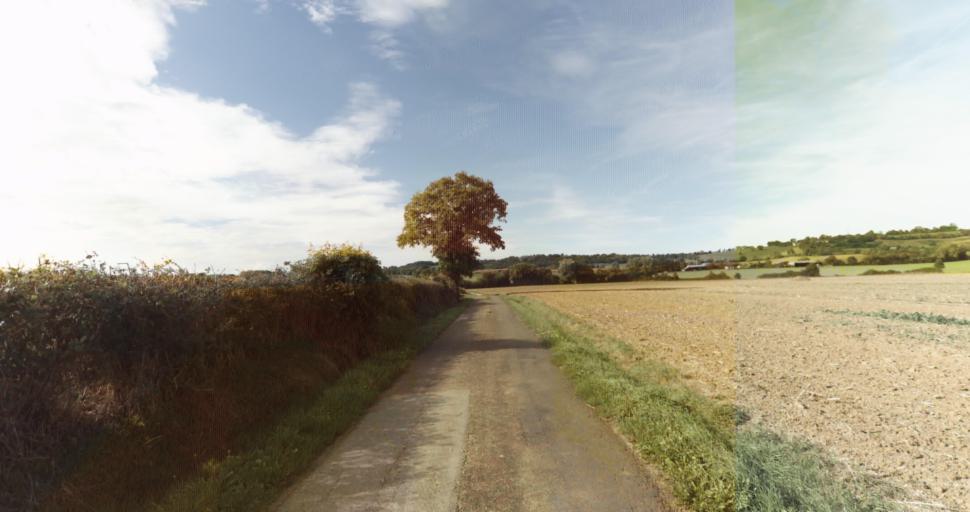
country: FR
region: Lower Normandy
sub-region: Departement de l'Orne
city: Gace
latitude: 48.7172
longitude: 0.2656
